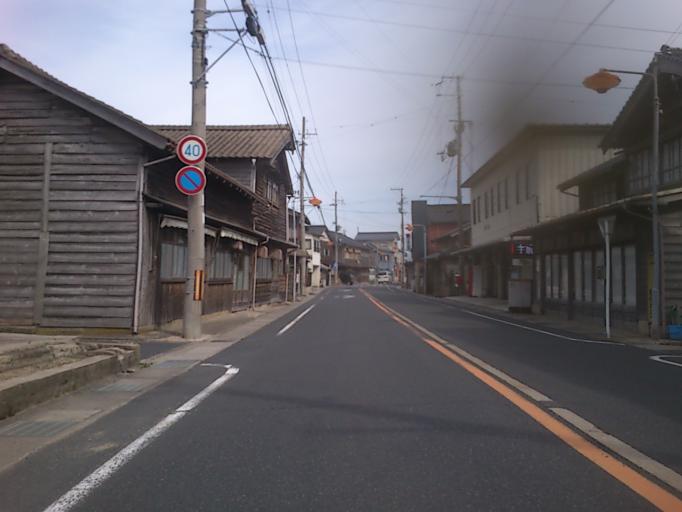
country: JP
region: Kyoto
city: Miyazu
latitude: 35.6877
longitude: 135.0215
